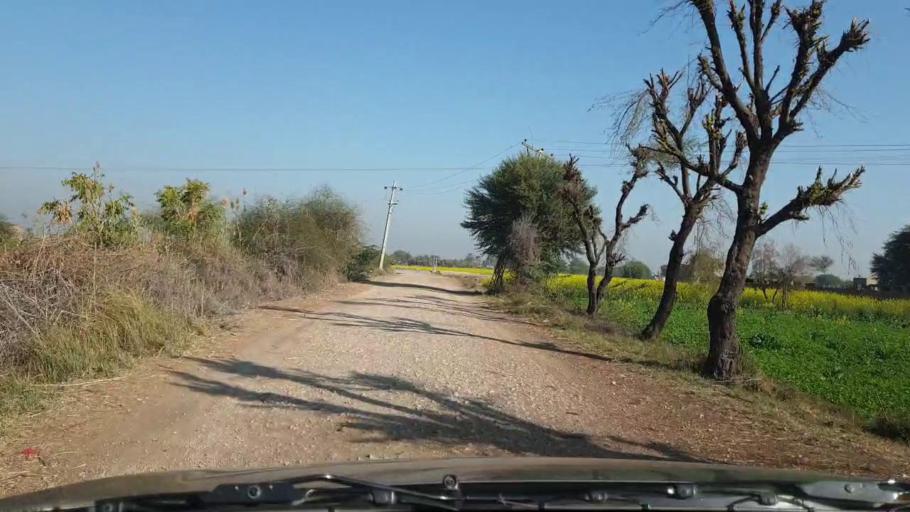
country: PK
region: Sindh
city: Jhol
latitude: 25.9449
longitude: 68.8380
